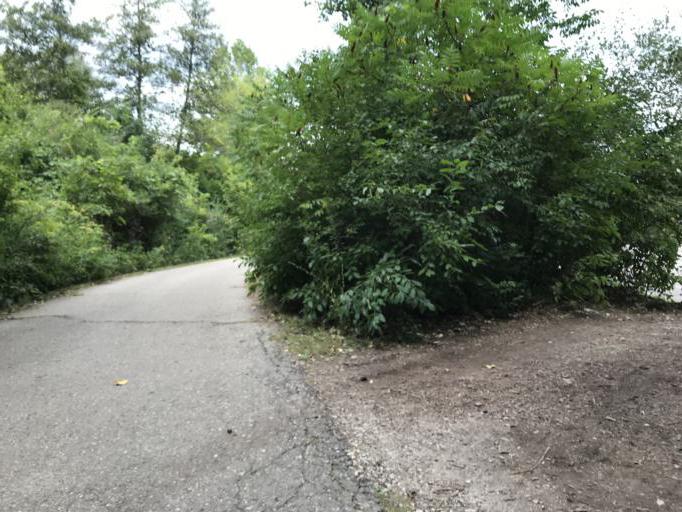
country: US
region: Michigan
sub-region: Washtenaw County
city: Ann Arbor
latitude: 42.3009
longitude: -83.7451
